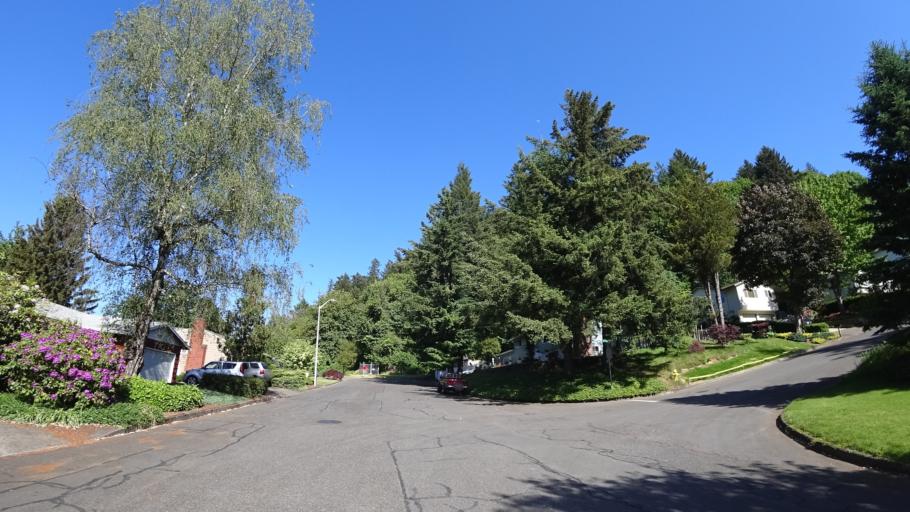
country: US
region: Oregon
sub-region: Multnomah County
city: Gresham
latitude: 45.5019
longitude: -122.4711
